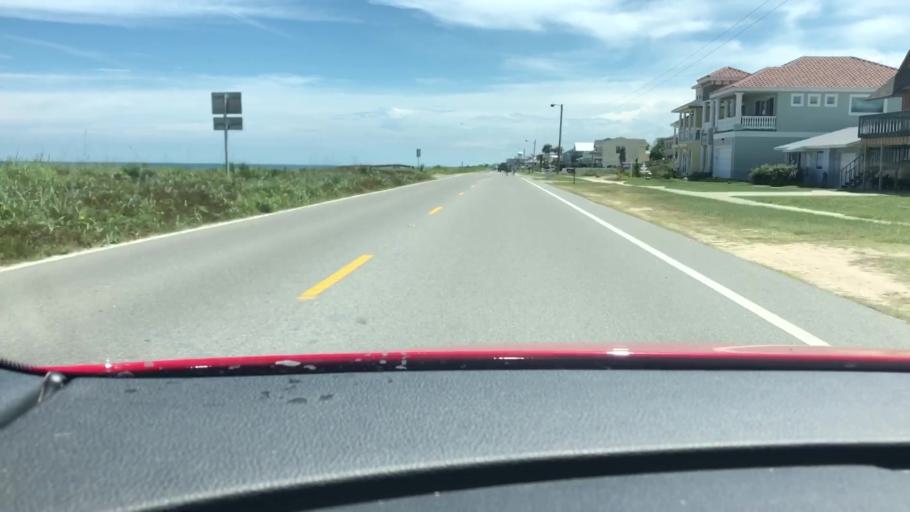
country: US
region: Florida
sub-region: Flagler County
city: Flagler Beach
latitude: 29.4543
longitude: -81.1149
